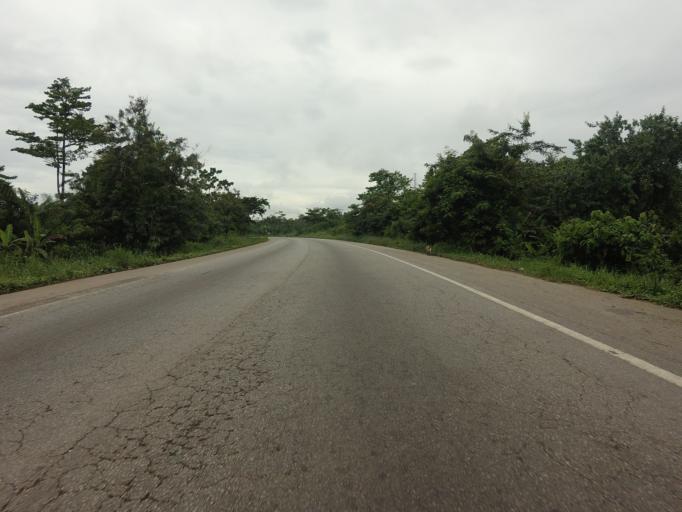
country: GH
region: Eastern
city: Nkawkaw
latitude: 6.4392
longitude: -0.5871
